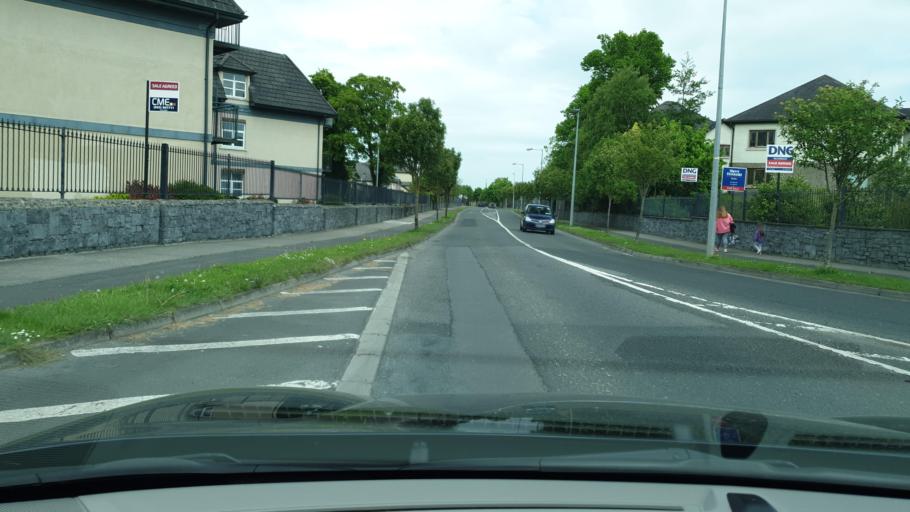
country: IE
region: Leinster
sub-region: Kildare
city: Clane
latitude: 53.2901
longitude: -6.6806
